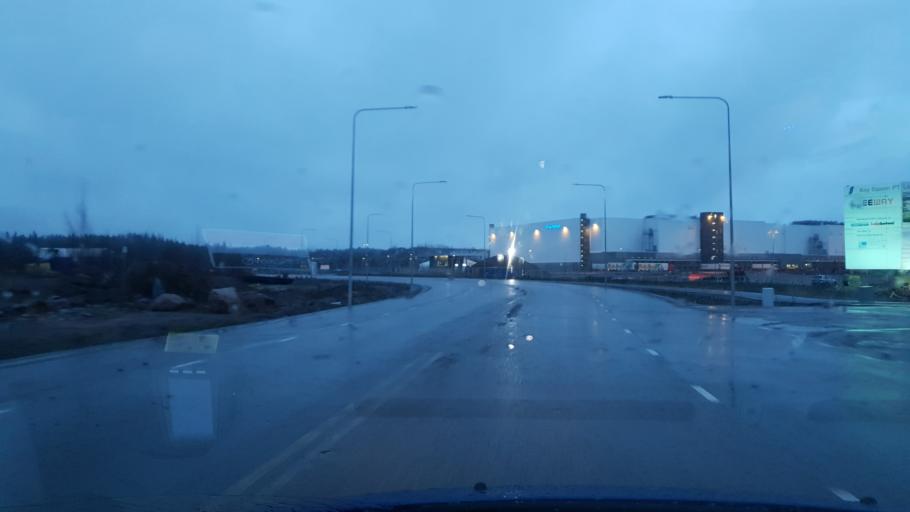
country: FI
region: Uusimaa
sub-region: Helsinki
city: Kerava
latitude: 60.3794
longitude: 25.1664
